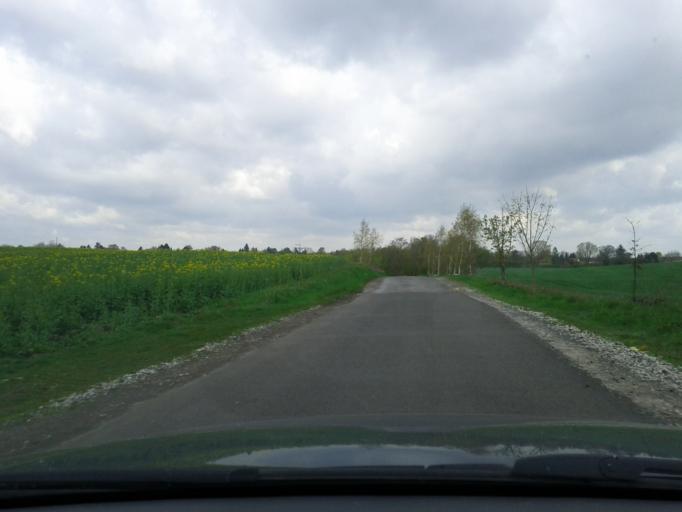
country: DE
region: Brandenburg
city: Schoneiche
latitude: 52.4840
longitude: 13.6798
